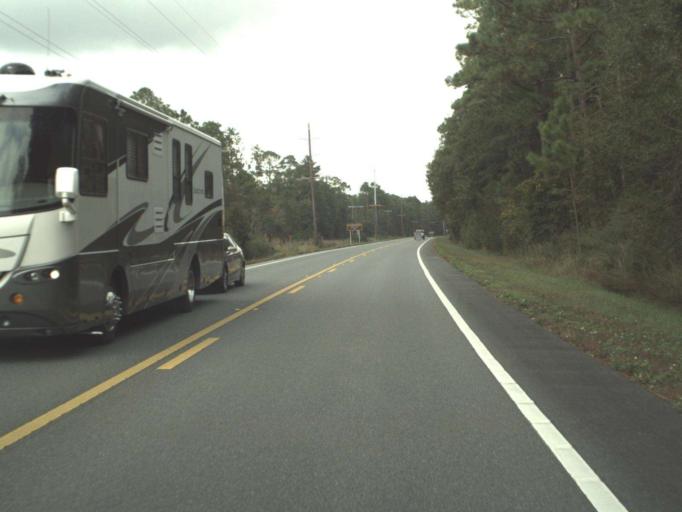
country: US
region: Florida
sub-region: Franklin County
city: Carrabelle
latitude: 29.9970
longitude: -84.5039
